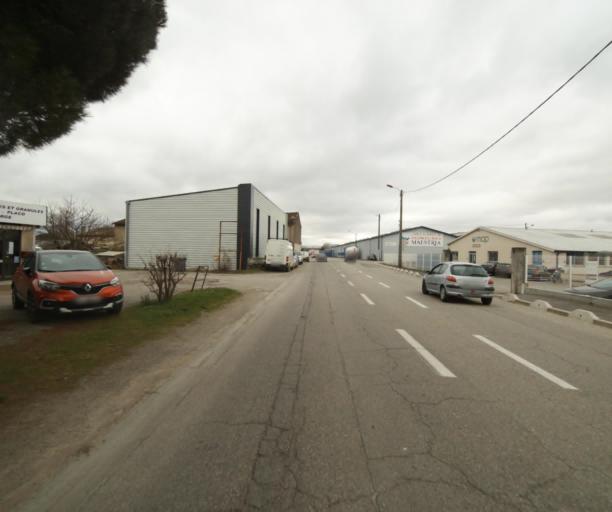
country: FR
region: Midi-Pyrenees
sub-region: Departement de l'Ariege
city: Pamiers
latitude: 43.1221
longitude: 1.6211
